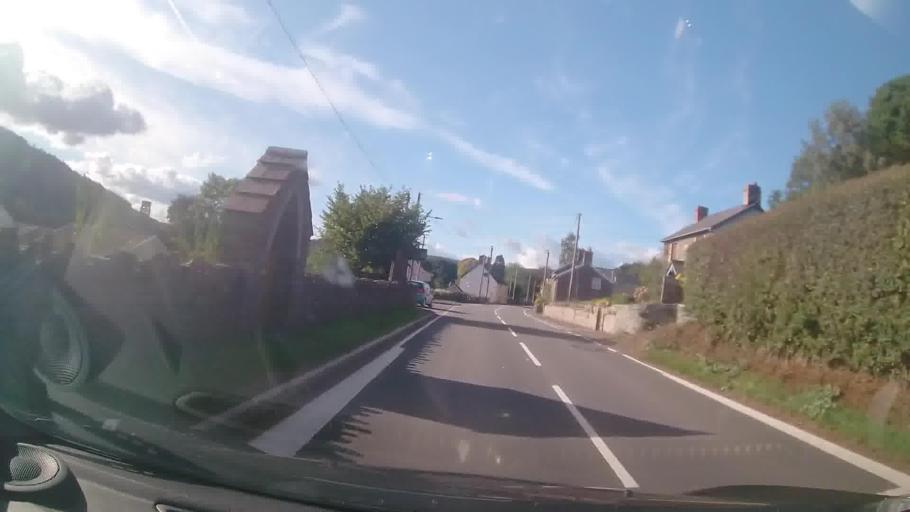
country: GB
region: Wales
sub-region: Blaenau Gwent
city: Brynmawr
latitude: 51.8842
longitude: -3.1822
